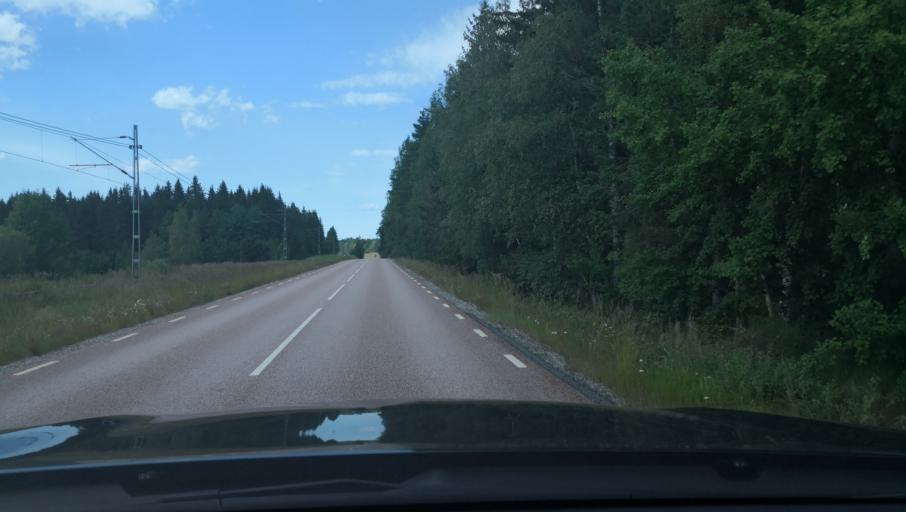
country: SE
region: Vaestmanland
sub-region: Surahammars Kommun
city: Ramnas
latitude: 59.8339
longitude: 16.1324
